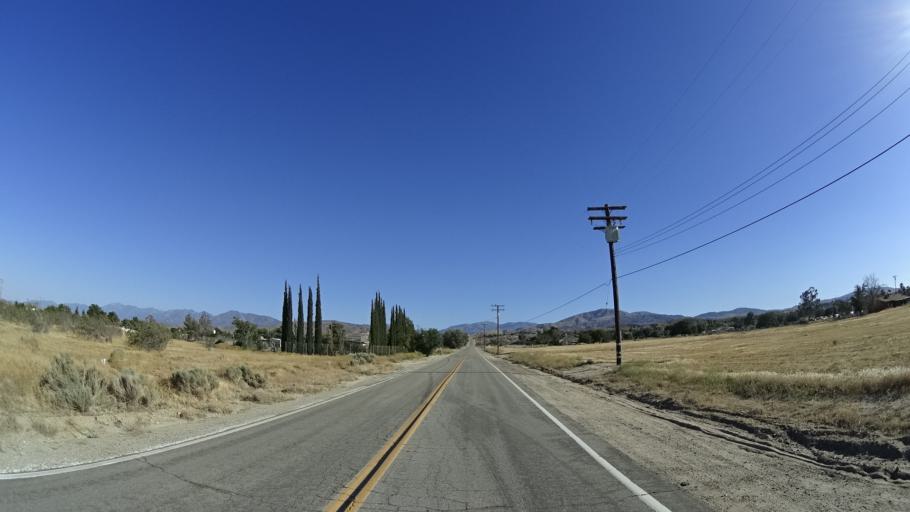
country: US
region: California
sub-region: Los Angeles County
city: Littlerock
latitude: 34.5400
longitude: -118.0277
